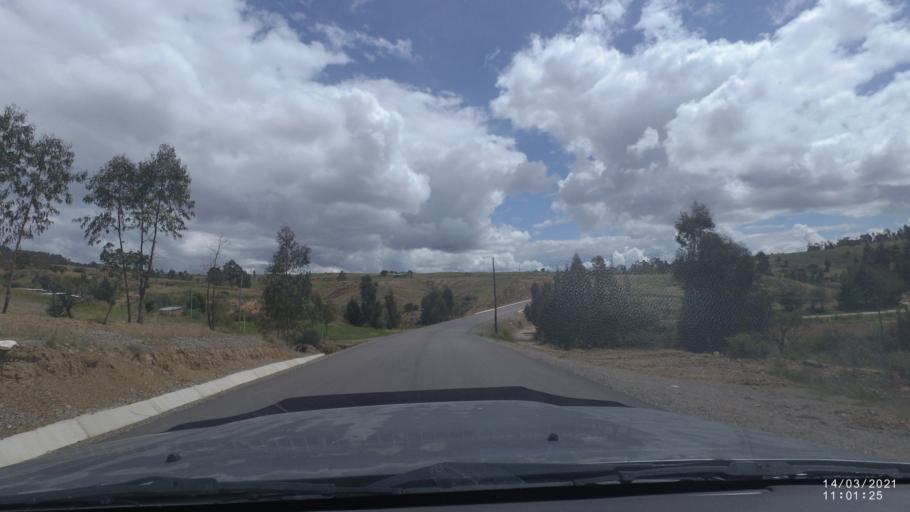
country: BO
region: Cochabamba
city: Tarata
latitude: -17.7947
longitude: -65.9637
